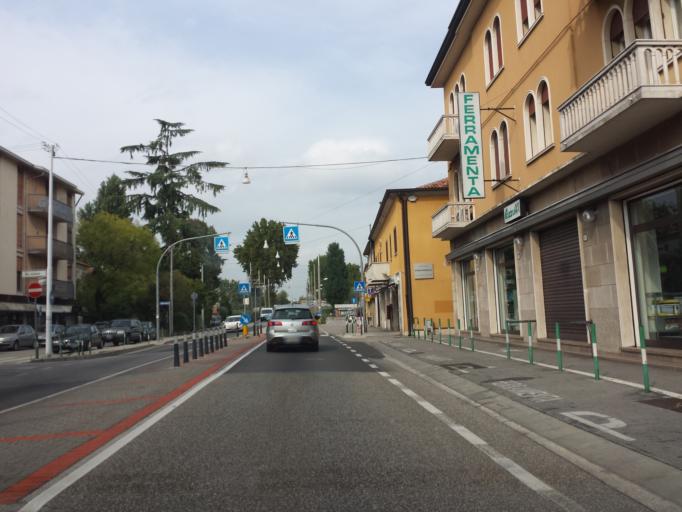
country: IT
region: Veneto
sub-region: Provincia di Padova
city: Vigodarzere
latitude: 45.4443
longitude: 11.8936
